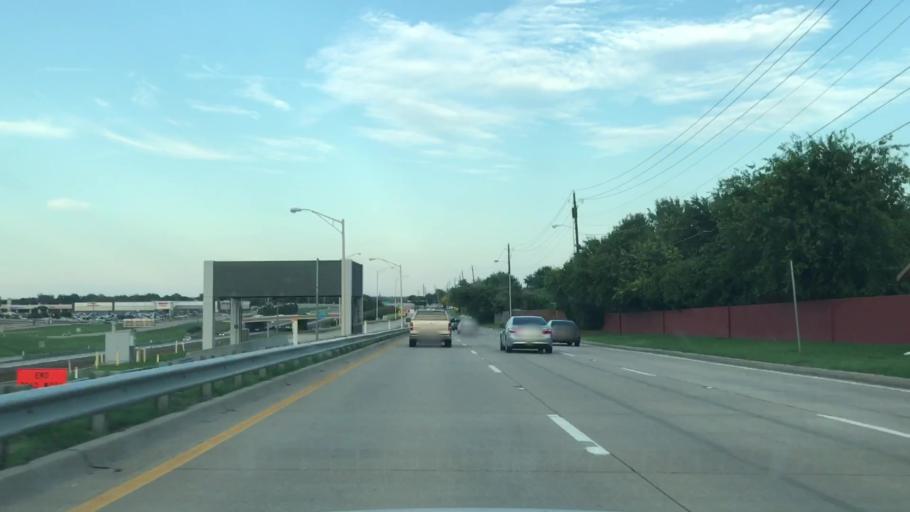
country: US
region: Texas
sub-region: Dallas County
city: Carrollton
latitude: 32.9832
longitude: -96.8959
